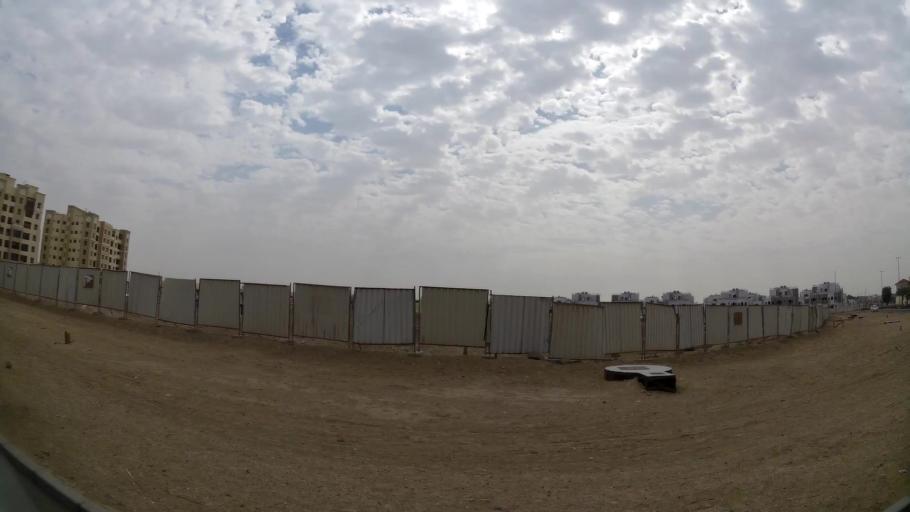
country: AE
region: Abu Dhabi
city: Abu Dhabi
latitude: 24.3104
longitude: 54.6204
